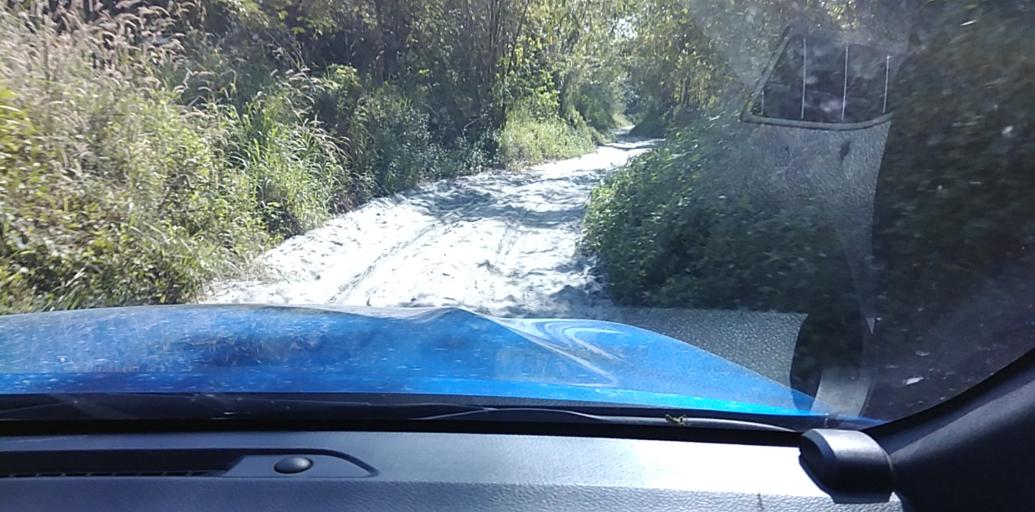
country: PH
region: Central Luzon
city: Santol
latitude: 15.1705
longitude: 120.4801
